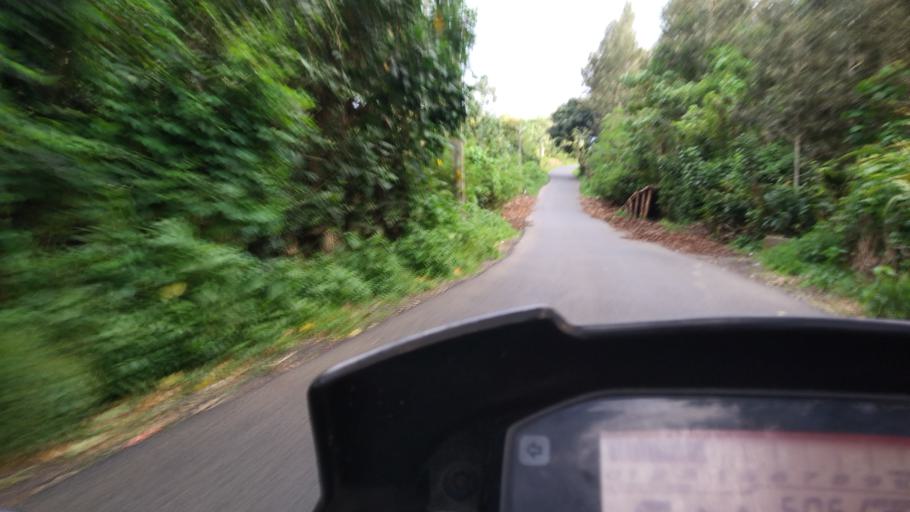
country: IN
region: Tamil Nadu
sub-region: Theni
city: Bodinayakkanur
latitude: 10.0352
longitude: 77.2234
